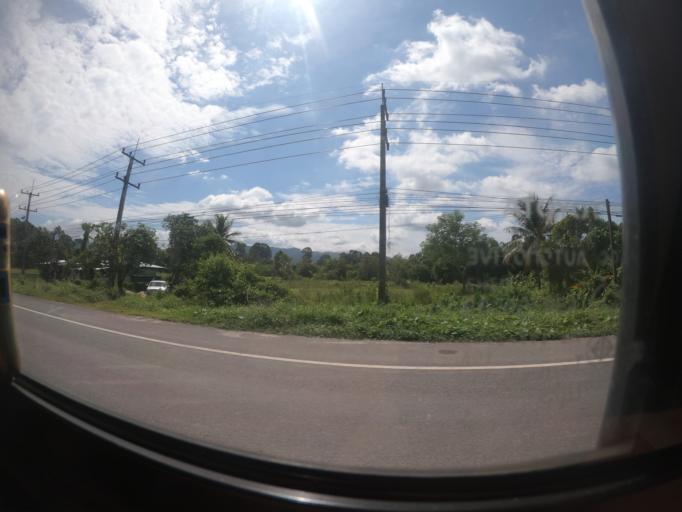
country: TH
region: Nakhon Nayok
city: Nakhon Nayok
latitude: 14.2760
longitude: 101.2931
